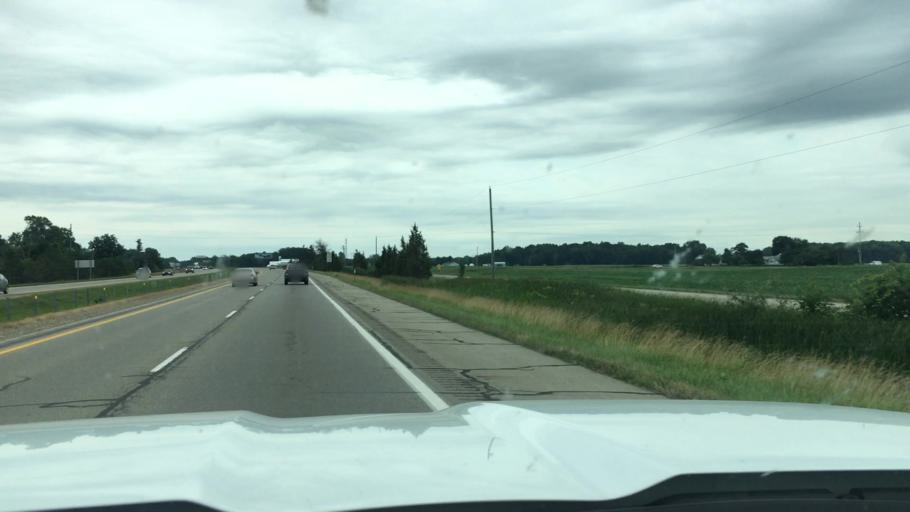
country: US
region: Michigan
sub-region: Allegan County
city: Wayland
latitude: 42.6231
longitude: -85.6626
